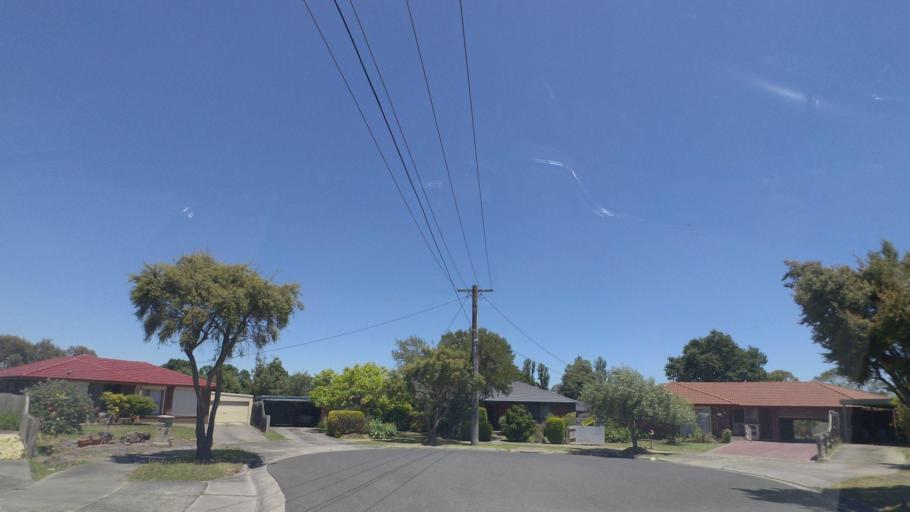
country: AU
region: Victoria
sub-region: Knox
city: Boronia
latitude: -37.8801
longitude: 145.2745
